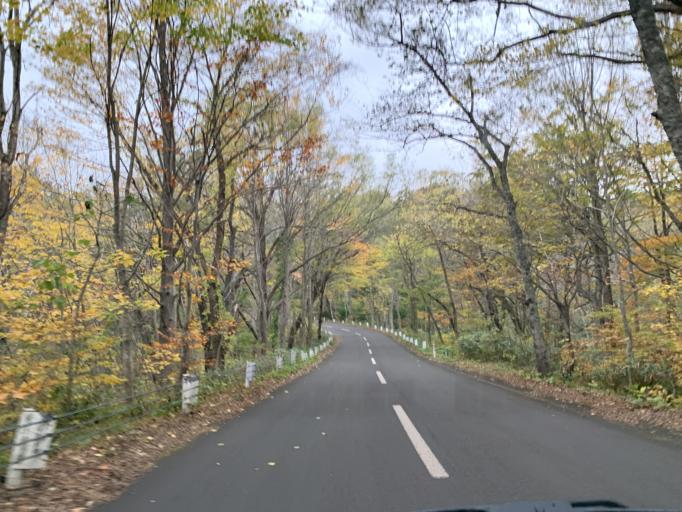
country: JP
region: Iwate
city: Mizusawa
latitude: 39.1046
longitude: 140.8677
